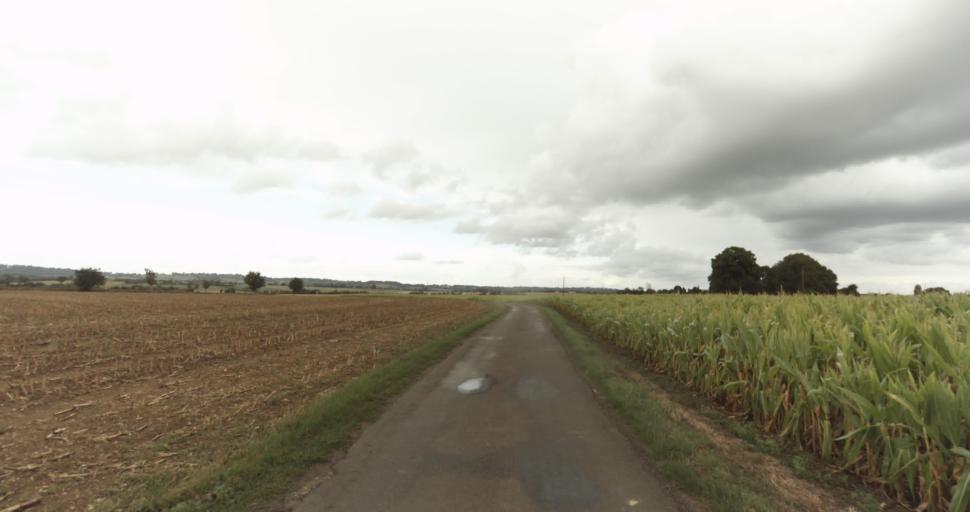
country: FR
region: Lower Normandy
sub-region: Departement de l'Orne
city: Gace
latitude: 48.6956
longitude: 0.2509
